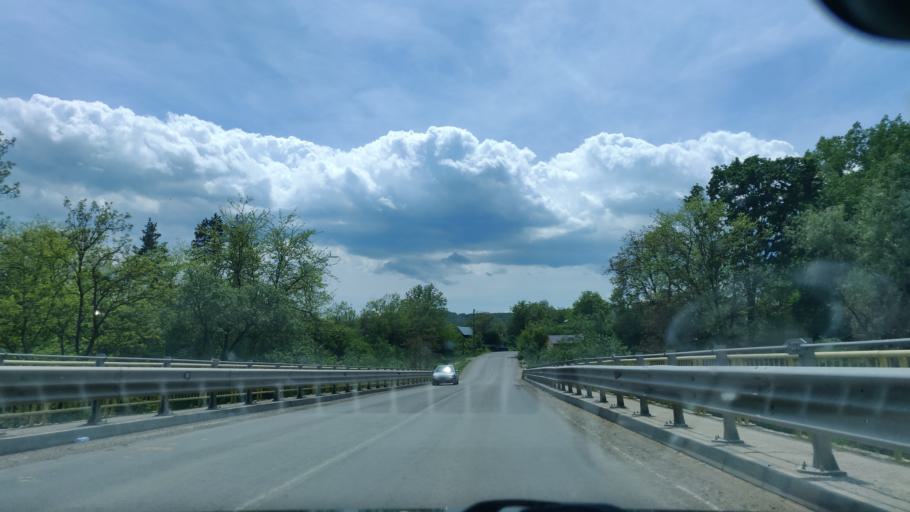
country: RO
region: Vrancea
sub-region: Comuna Vidra
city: Vidra
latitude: 45.9050
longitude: 26.8931
